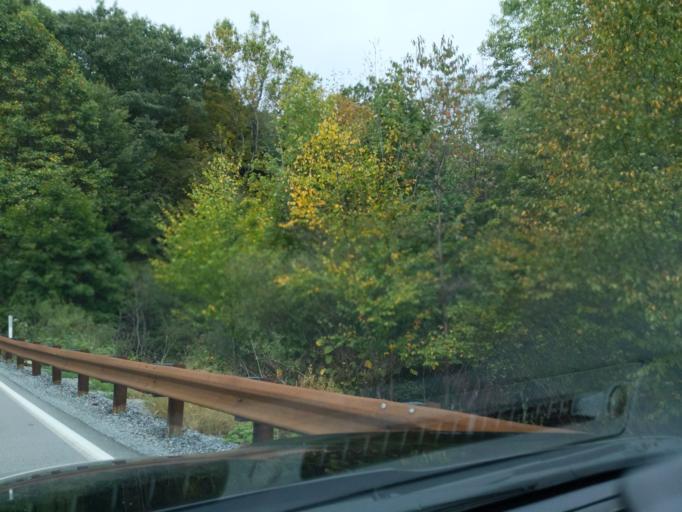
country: US
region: Pennsylvania
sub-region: Blair County
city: Altoona
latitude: 40.4963
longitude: -78.4619
